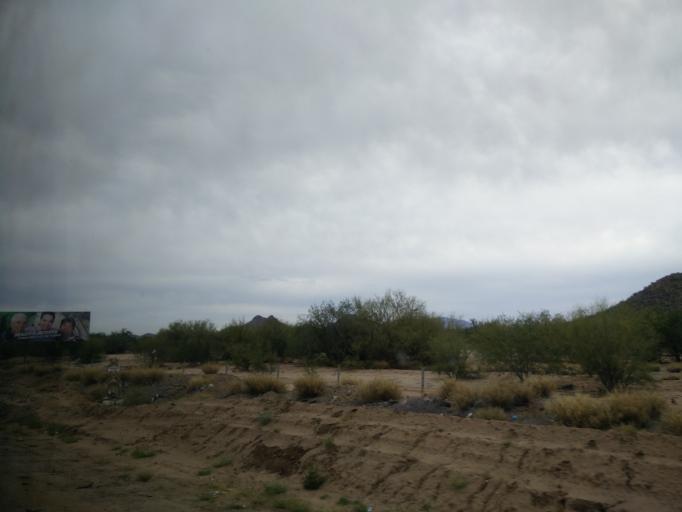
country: MX
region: Sonora
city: Hermosillo
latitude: 28.8529
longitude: -110.9584
